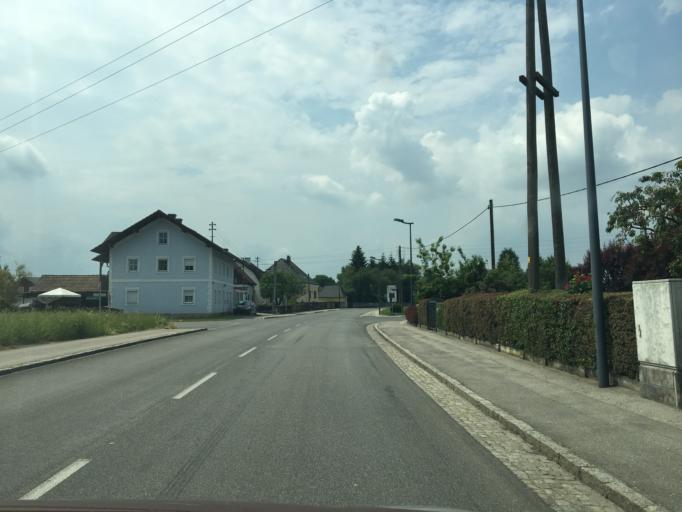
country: AT
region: Upper Austria
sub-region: Politischer Bezirk Braunau am Inn
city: Braunau am Inn
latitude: 48.1882
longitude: 13.1262
